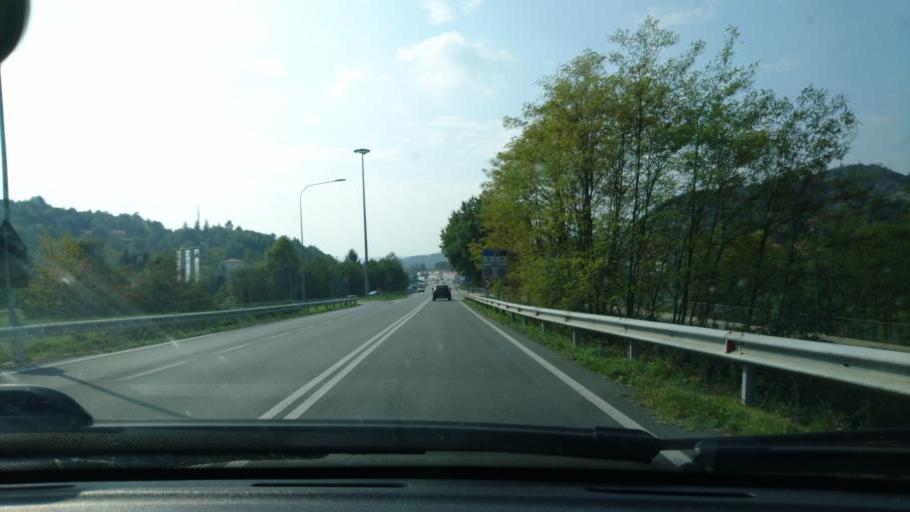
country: IT
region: Liguria
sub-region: Provincia di Savona
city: Cairo Montenotte
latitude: 44.3944
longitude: 8.2823
